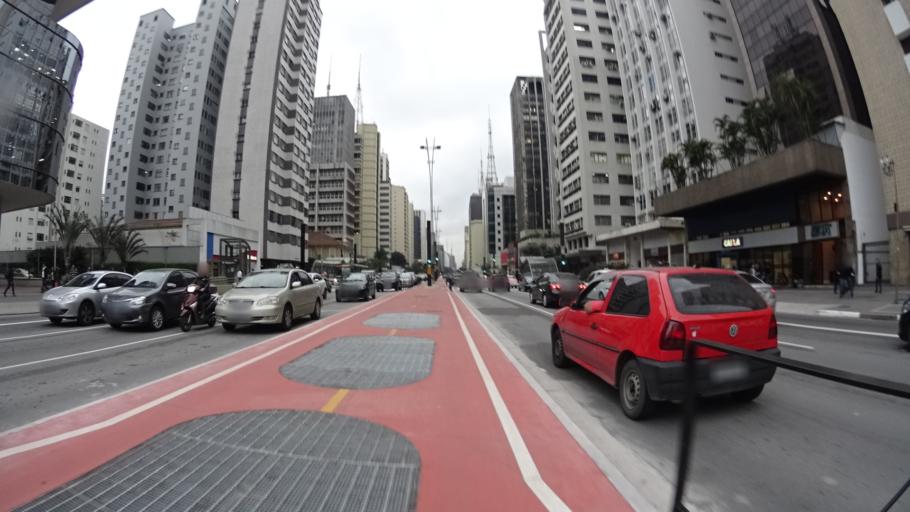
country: BR
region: Sao Paulo
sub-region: Sao Paulo
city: Sao Paulo
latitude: -23.5695
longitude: -46.6466
